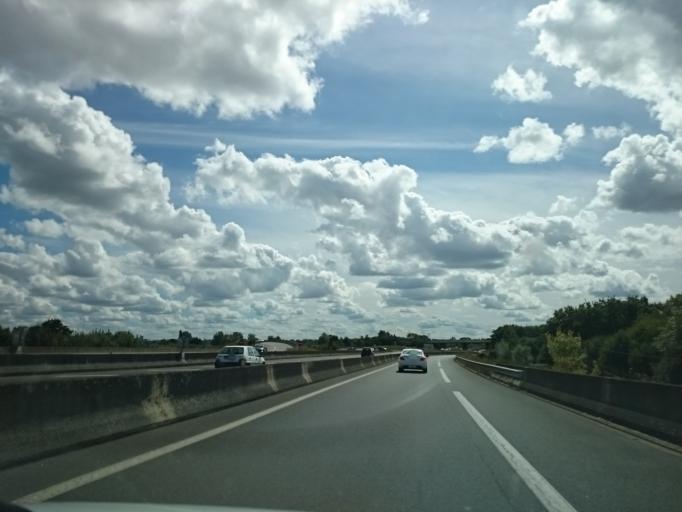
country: FR
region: Pays de la Loire
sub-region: Departement de la Loire-Atlantique
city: Sainte-Luce-sur-Loire
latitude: 47.2400
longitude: -1.4778
